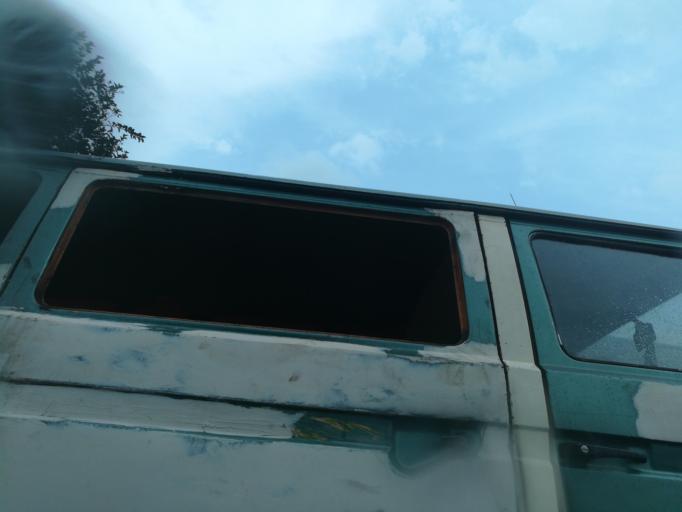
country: NG
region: Lagos
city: Oshodi
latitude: 6.5776
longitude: 3.3404
